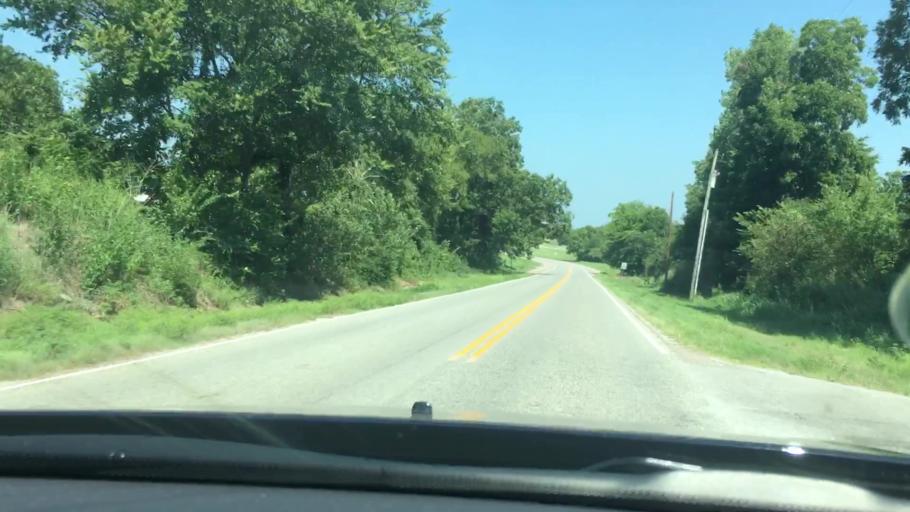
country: US
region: Oklahoma
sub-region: Johnston County
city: Tishomingo
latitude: 34.2435
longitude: -96.5487
